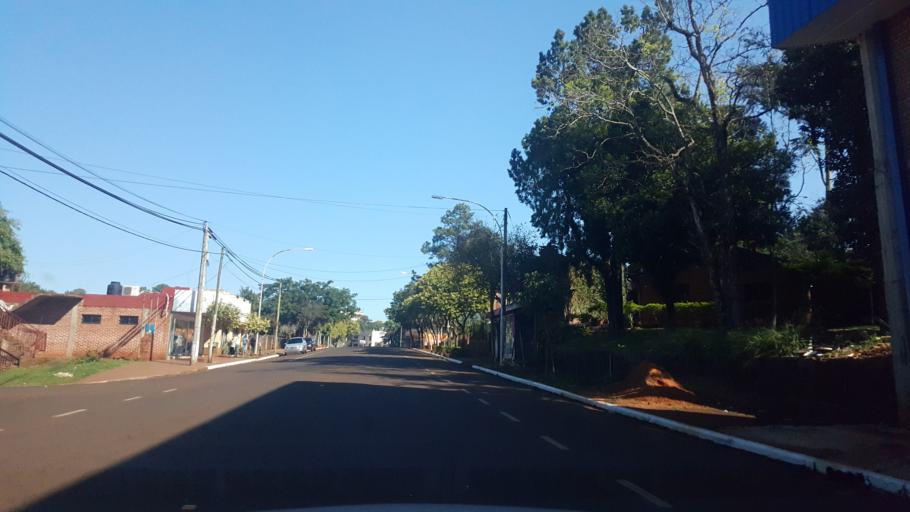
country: AR
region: Misiones
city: Puerto Rico
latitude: -26.8035
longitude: -55.0217
